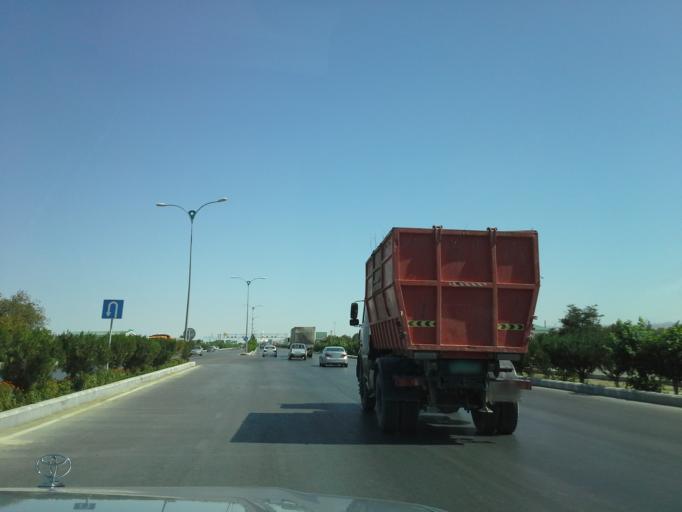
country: TM
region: Ahal
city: Annau
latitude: 37.9102
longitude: 58.5014
